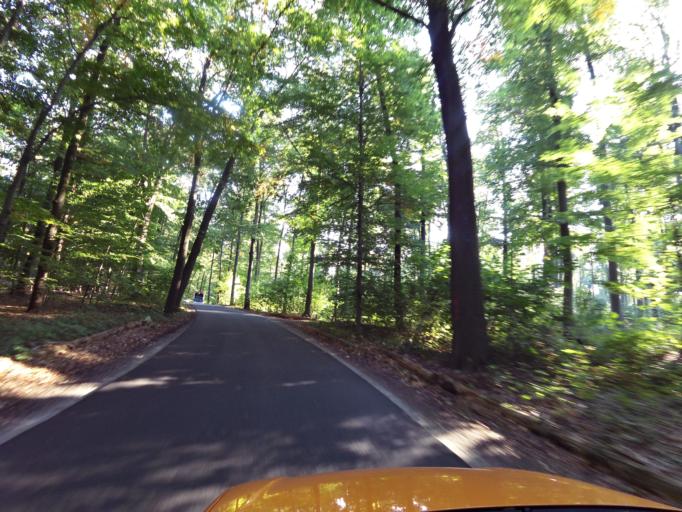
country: DE
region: Brandenburg
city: Potsdam
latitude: 52.4530
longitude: 13.0631
